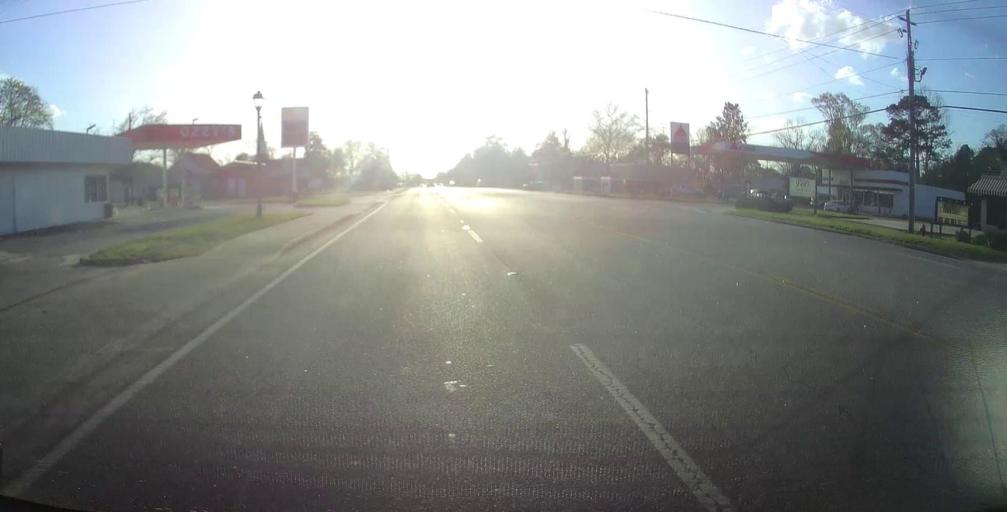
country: US
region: Georgia
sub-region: Evans County
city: Claxton
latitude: 32.1589
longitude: -81.9329
